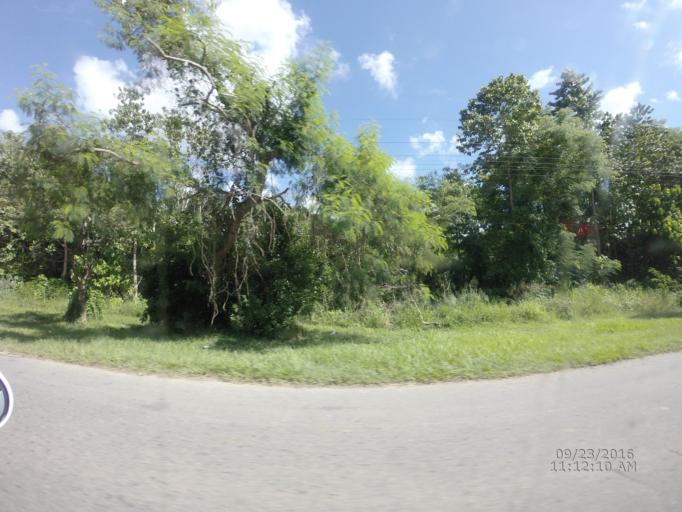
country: CU
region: La Habana
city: Arroyo Naranjo
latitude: 23.0283
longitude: -82.2797
